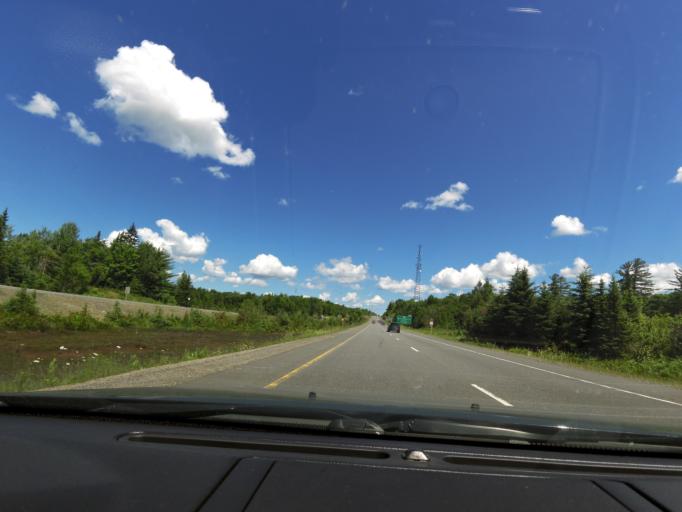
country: CA
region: Ontario
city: Bracebridge
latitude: 45.1988
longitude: -79.3138
